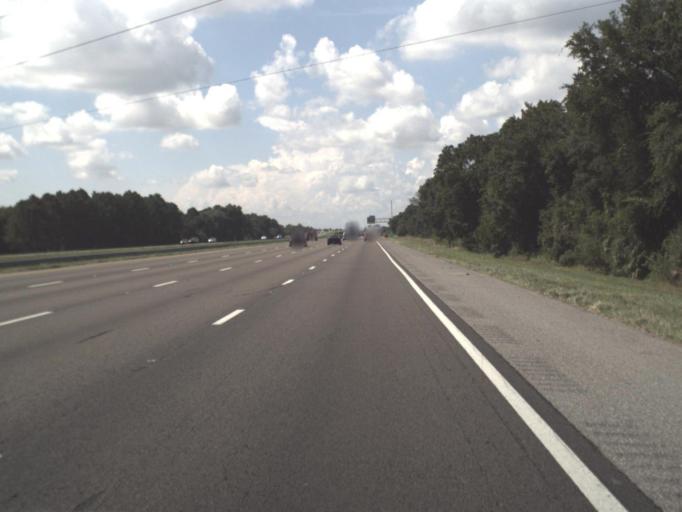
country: US
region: Florida
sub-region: Hillsborough County
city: Riverview
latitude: 27.8752
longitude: -82.3481
